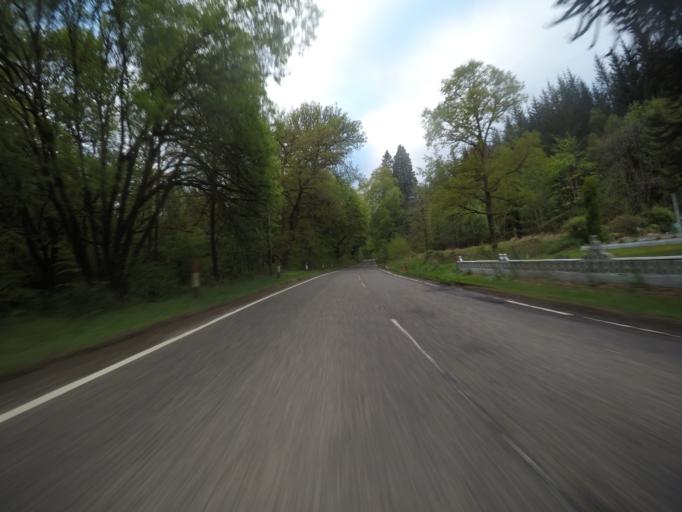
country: GB
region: Scotland
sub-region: Highland
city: Spean Bridge
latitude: 57.0733
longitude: -4.7705
